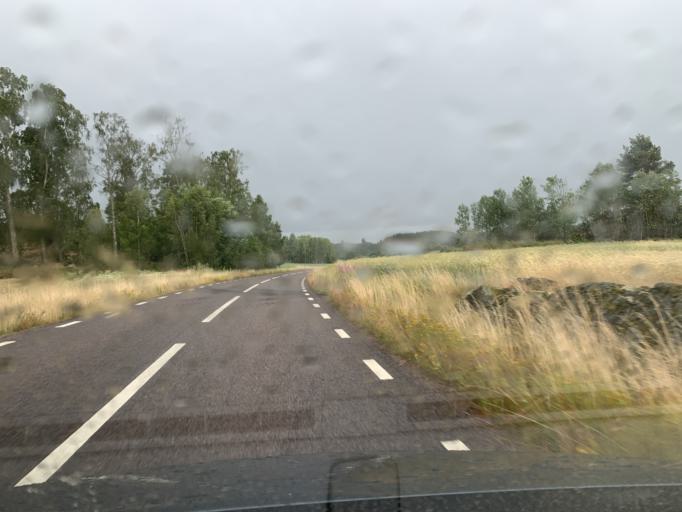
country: SE
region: Kalmar
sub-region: Vasterviks Kommun
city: Overum
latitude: 57.9997
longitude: 16.1780
